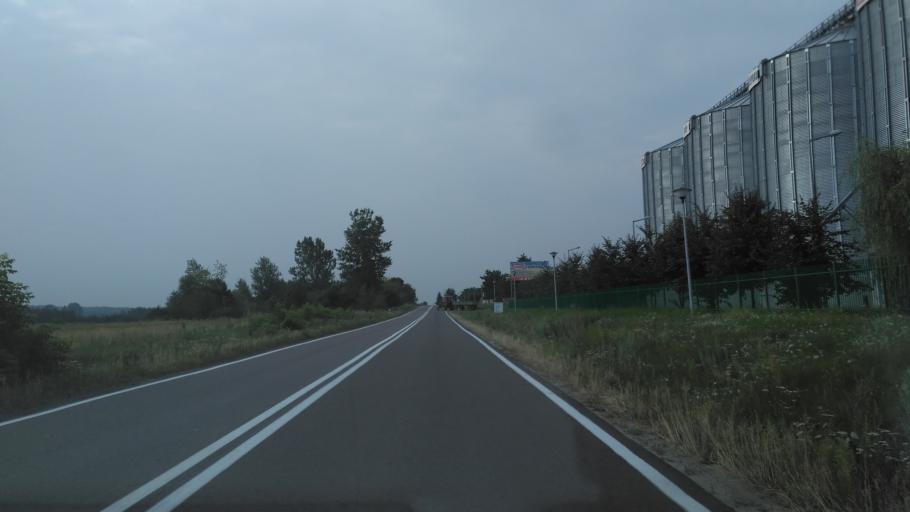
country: PL
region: Lublin Voivodeship
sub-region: Powiat chelmski
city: Rejowiec Fabryczny
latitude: 51.1833
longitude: 23.1739
